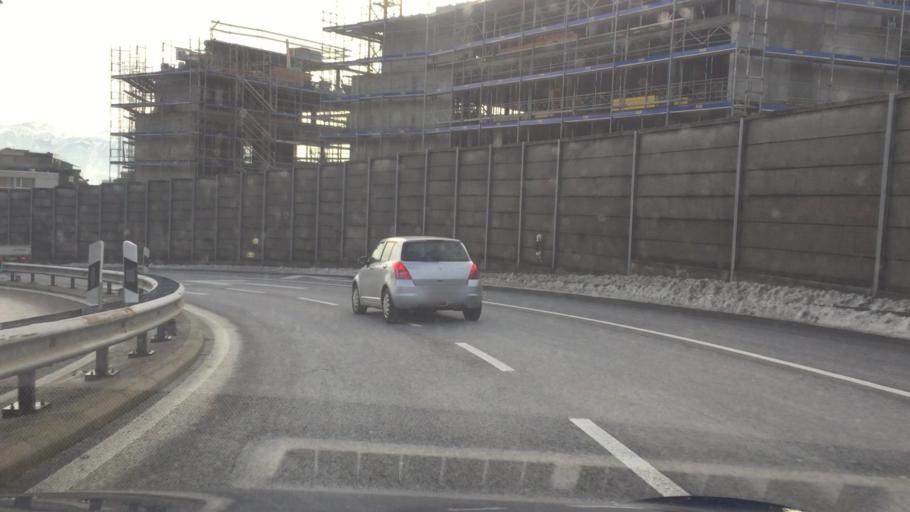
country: CH
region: Vaud
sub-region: Lausanne District
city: Epalinges
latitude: 46.5409
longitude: 6.6516
